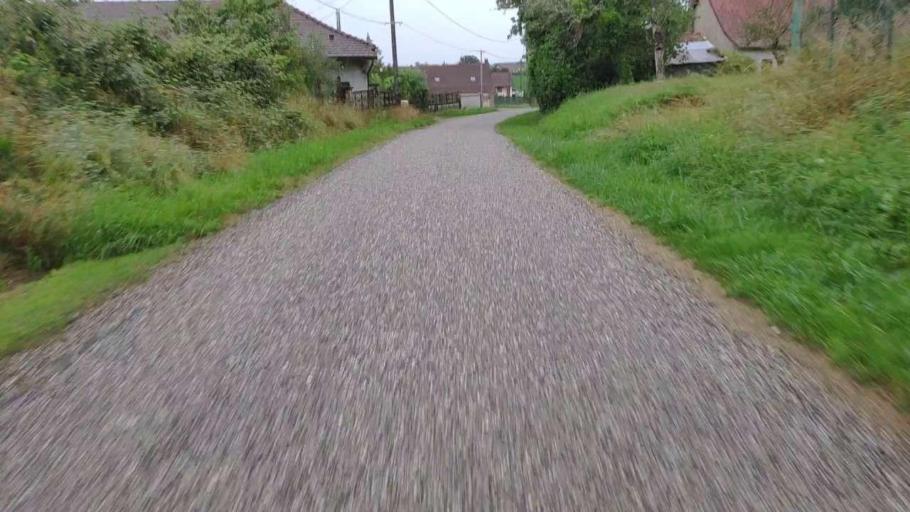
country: FR
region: Franche-Comte
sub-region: Departement du Jura
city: Chaussin
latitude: 46.8759
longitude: 5.4145
